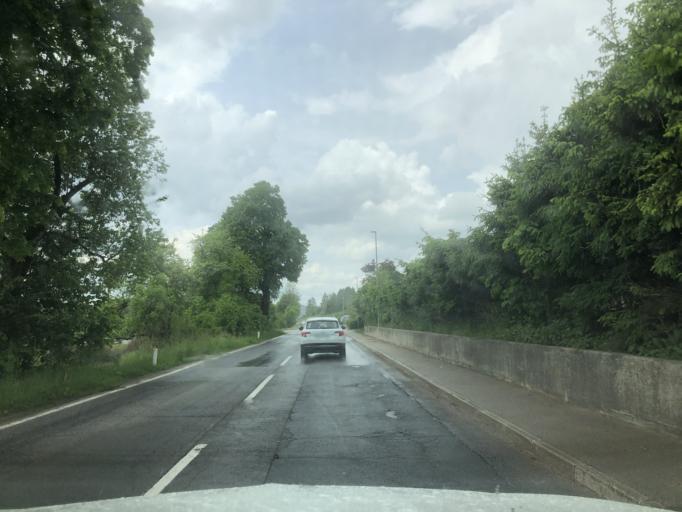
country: SI
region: Cerknica
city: Cerknica
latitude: 45.7874
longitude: 14.3747
